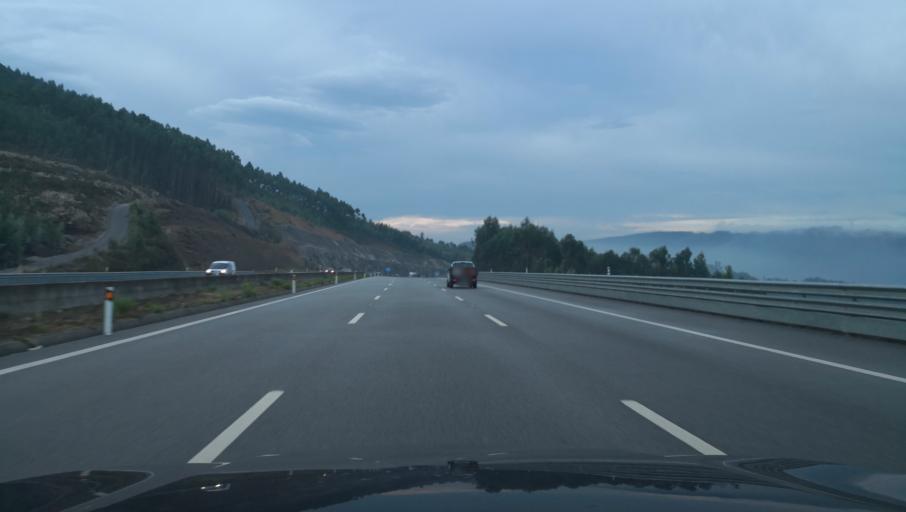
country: PT
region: Porto
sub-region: Paredes
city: Recarei
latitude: 41.1163
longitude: -8.4328
